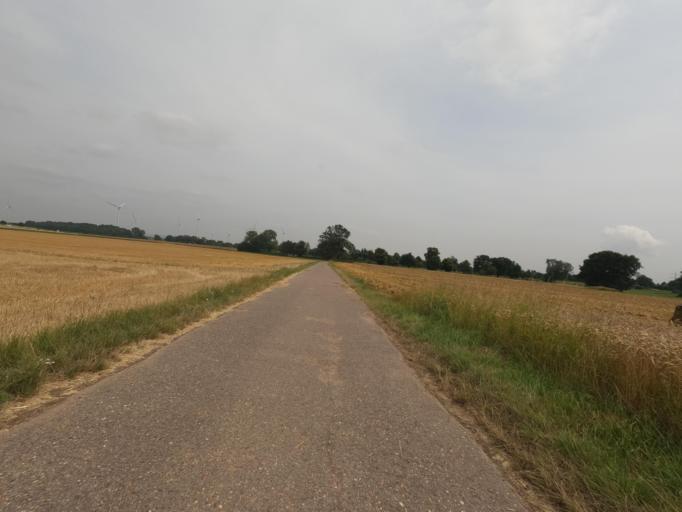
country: DE
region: North Rhine-Westphalia
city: Siersdorf
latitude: 50.9089
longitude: 6.2472
